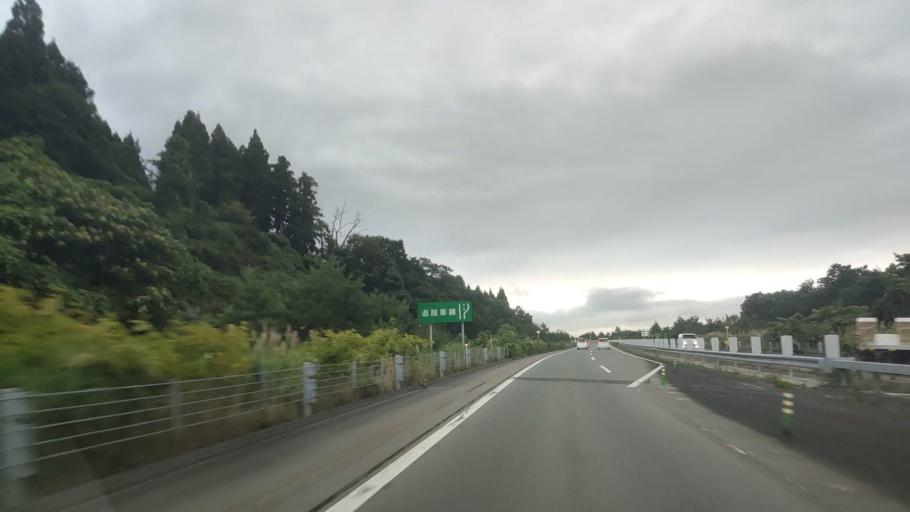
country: JP
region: Hokkaido
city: Nanae
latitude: 41.9072
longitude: 140.6965
